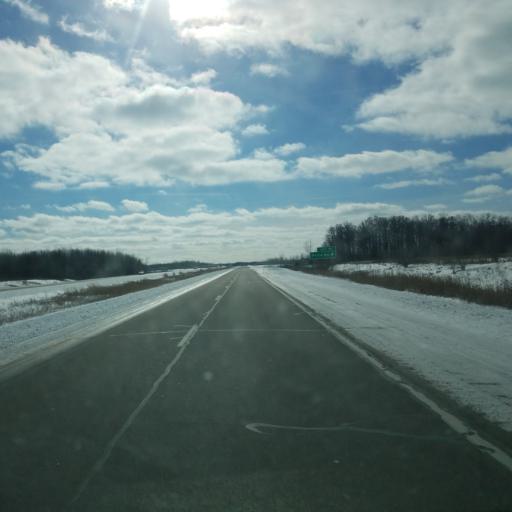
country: US
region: Michigan
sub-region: Clinton County
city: Saint Johns
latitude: 42.9393
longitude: -84.5189
